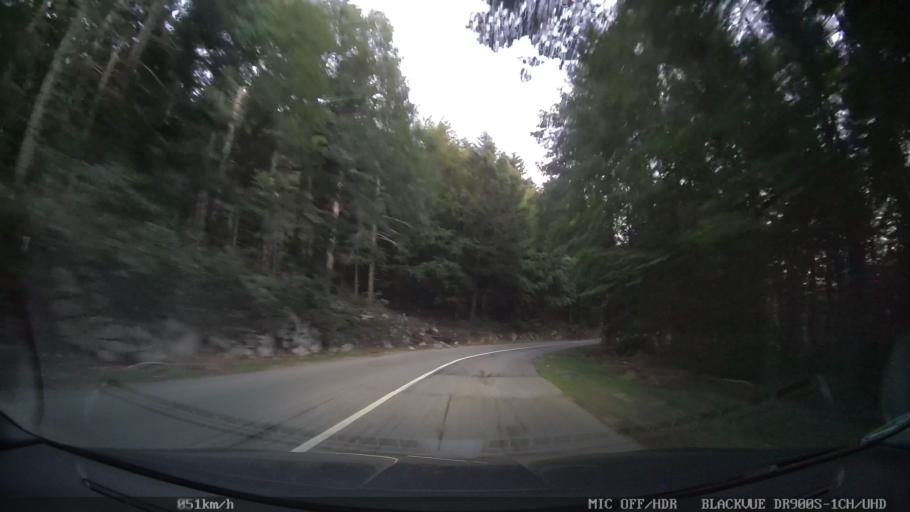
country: HR
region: Primorsko-Goranska
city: Novi Vinodolski
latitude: 45.1868
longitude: 14.8761
